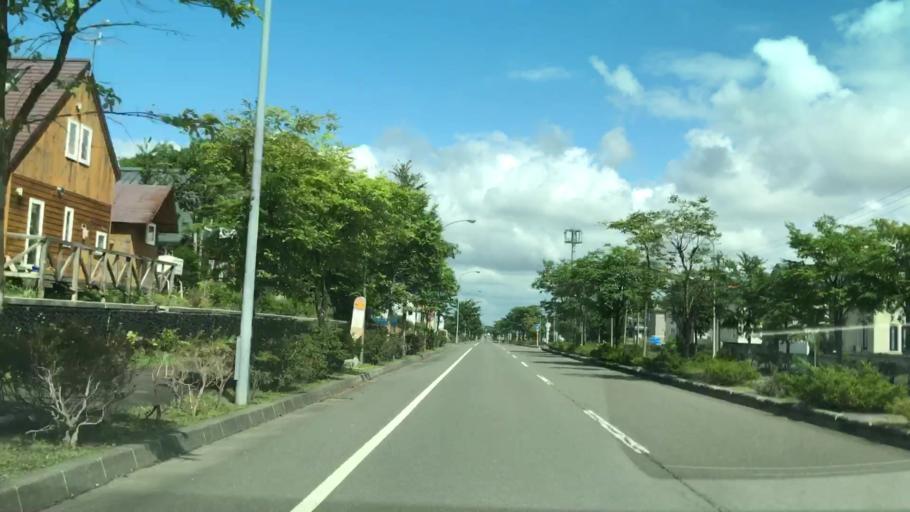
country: JP
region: Hokkaido
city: Chitose
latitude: 42.7759
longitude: 141.5995
